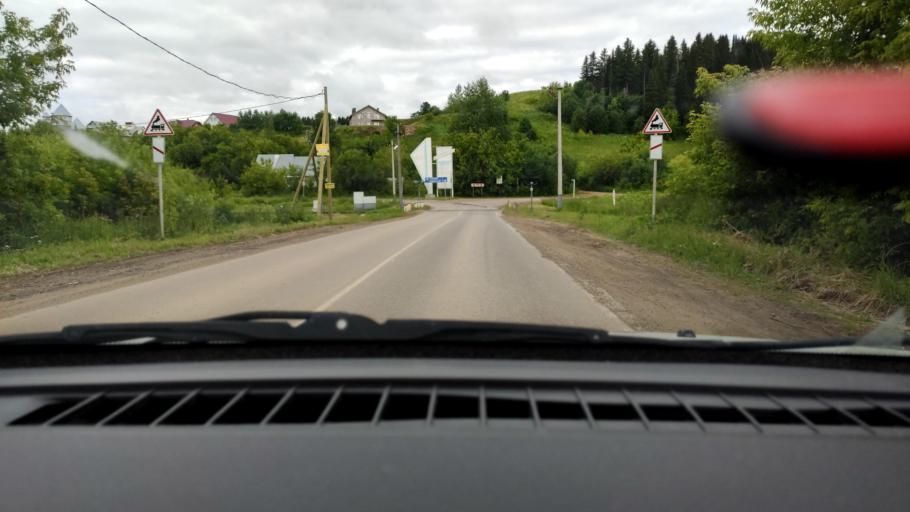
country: RU
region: Perm
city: Chaykovskaya
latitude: 58.1116
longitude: 55.5848
